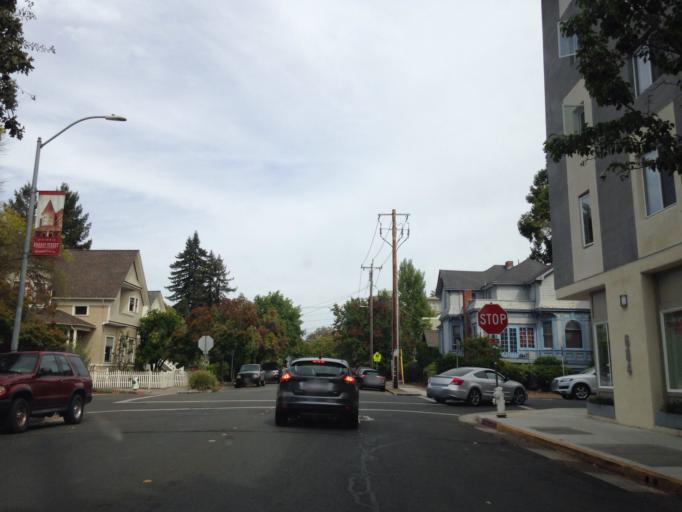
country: US
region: California
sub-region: Sonoma County
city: Santa Rosa
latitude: 38.4429
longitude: -122.7144
